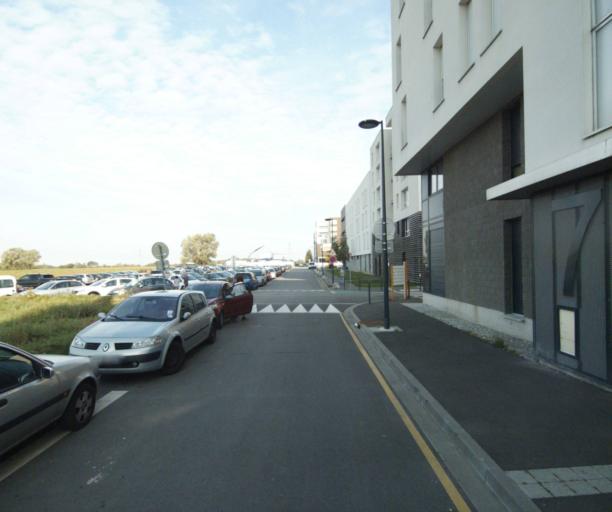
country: FR
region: Nord-Pas-de-Calais
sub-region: Departement du Nord
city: Capinghem
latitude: 50.6497
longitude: 2.9700
